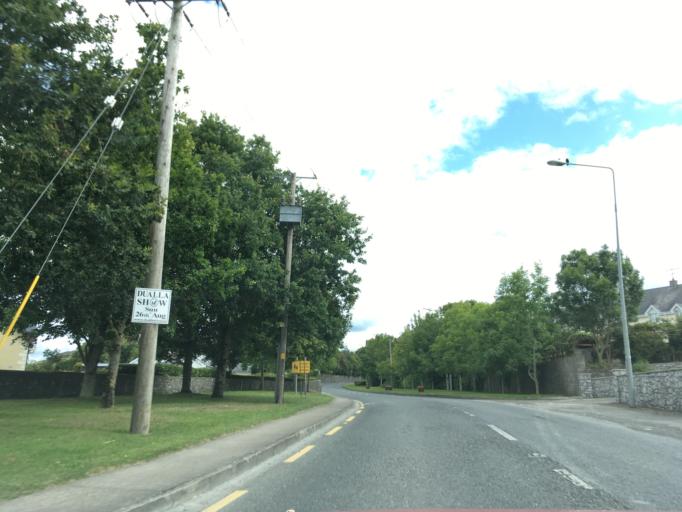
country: IE
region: Munster
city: Cashel
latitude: 52.5153
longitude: -7.8984
